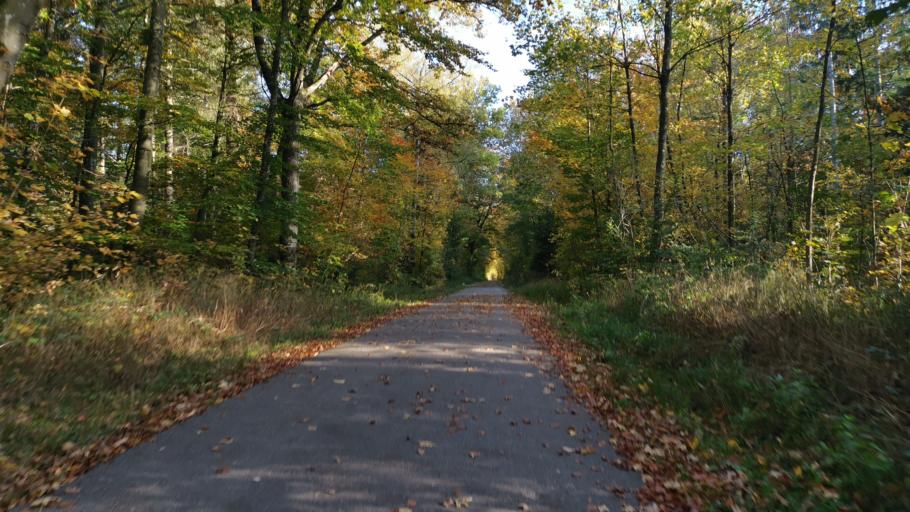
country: DE
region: Bavaria
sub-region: Upper Bavaria
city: Pullach im Isartal
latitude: 48.0696
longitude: 11.5502
